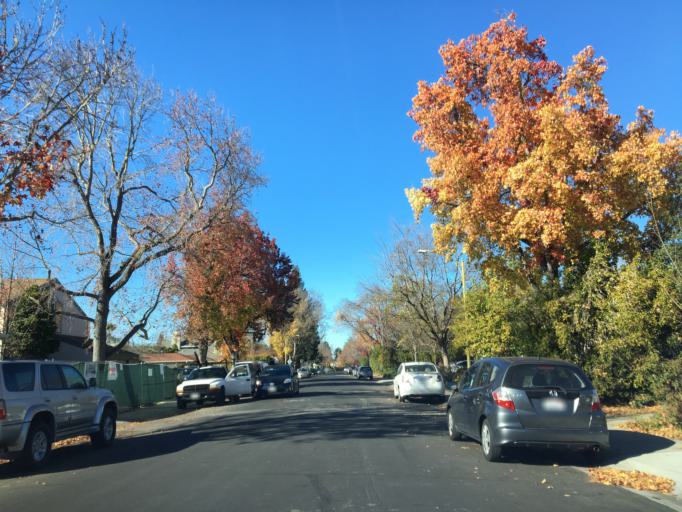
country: US
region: California
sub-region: Santa Clara County
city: Palo Alto
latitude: 37.4226
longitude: -122.1222
